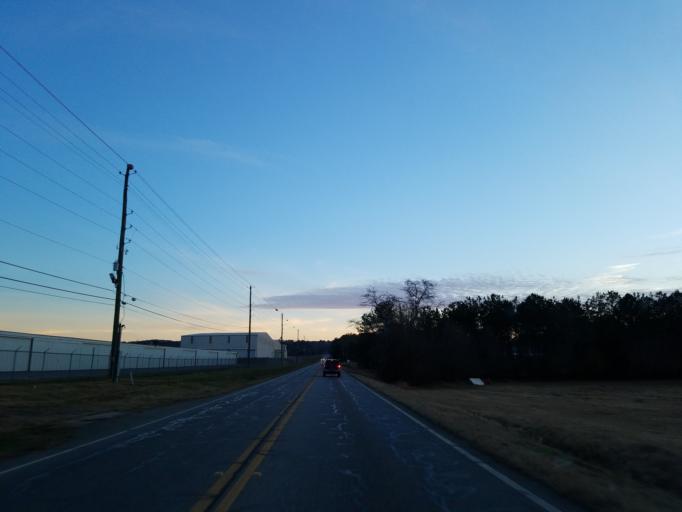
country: US
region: Georgia
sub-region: Bartow County
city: Cartersville
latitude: 34.1216
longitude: -84.8509
